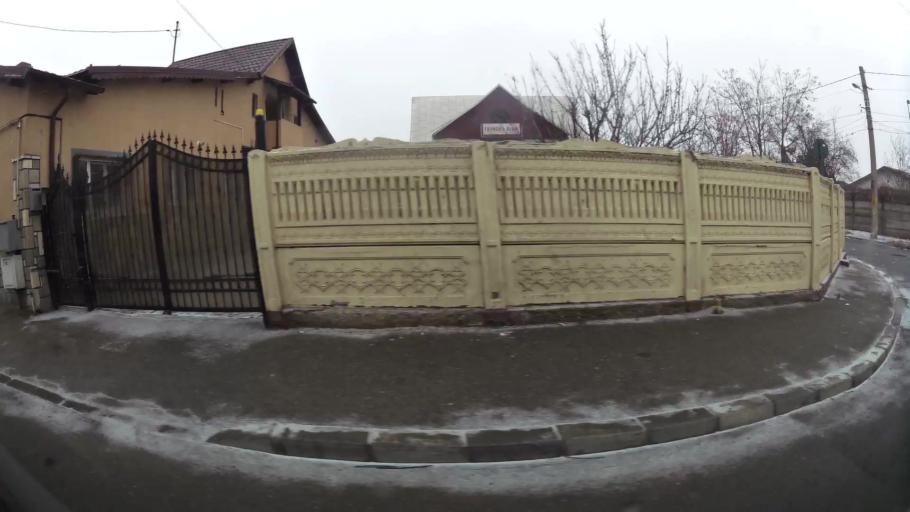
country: RO
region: Prahova
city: Ploiesti
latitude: 44.9549
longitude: 26.0416
